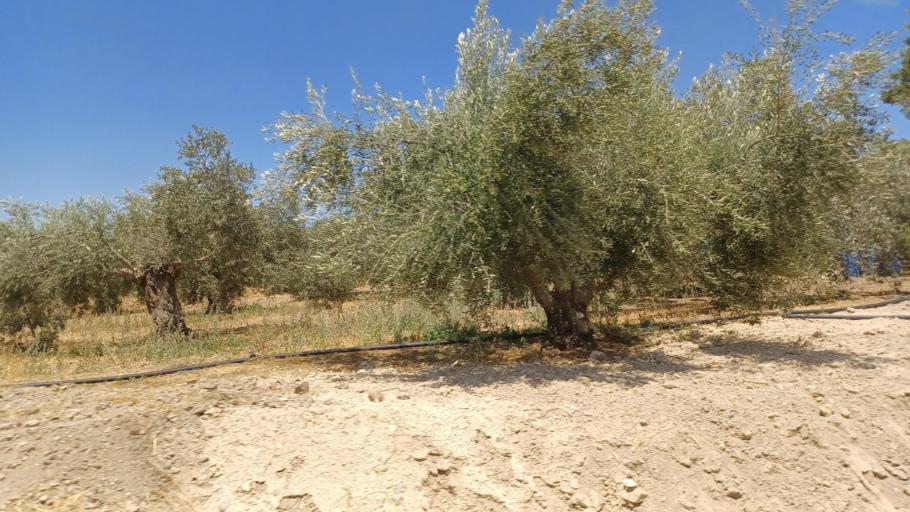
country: CY
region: Larnaka
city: Troulloi
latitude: 35.0401
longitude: 33.6170
